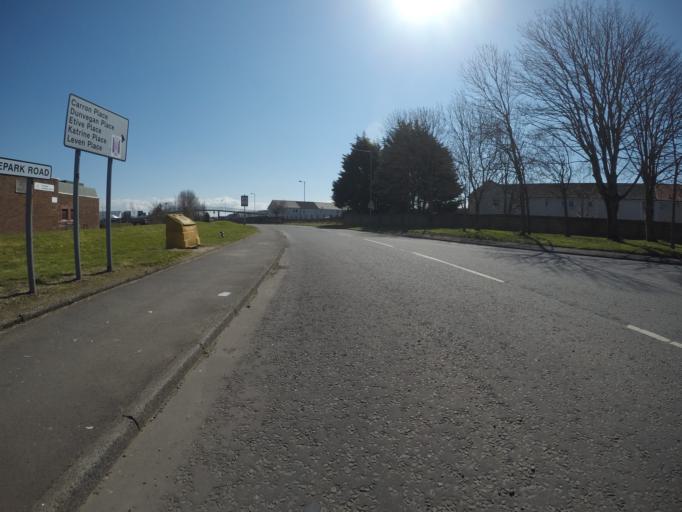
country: GB
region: Scotland
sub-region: North Ayrshire
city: Irvine
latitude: 55.6298
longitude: -4.6673
